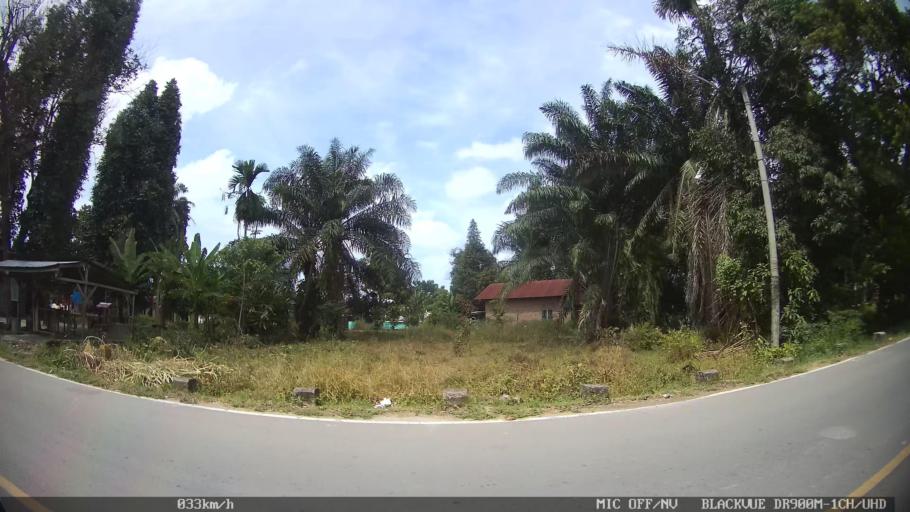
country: ID
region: North Sumatra
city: Percut
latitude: 3.6053
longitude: 98.8561
